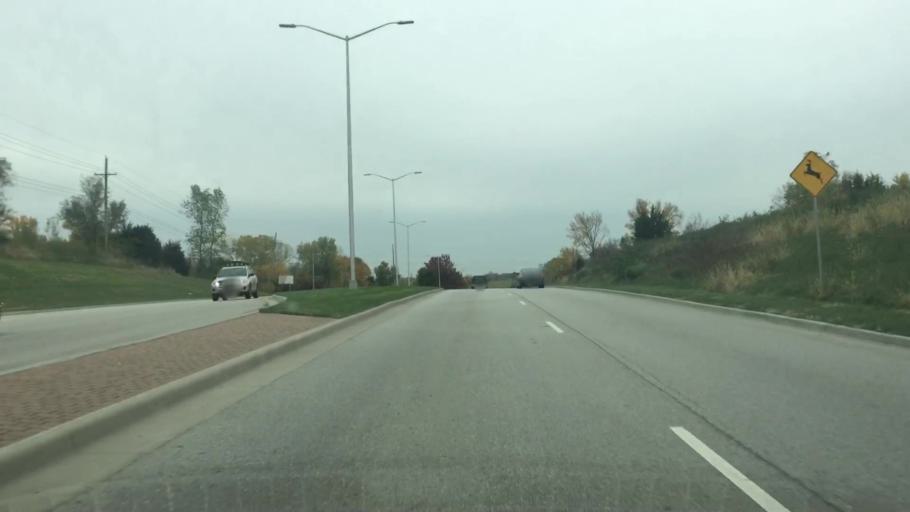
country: US
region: Kansas
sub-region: Johnson County
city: Lenexa
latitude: 38.9392
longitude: -94.7796
